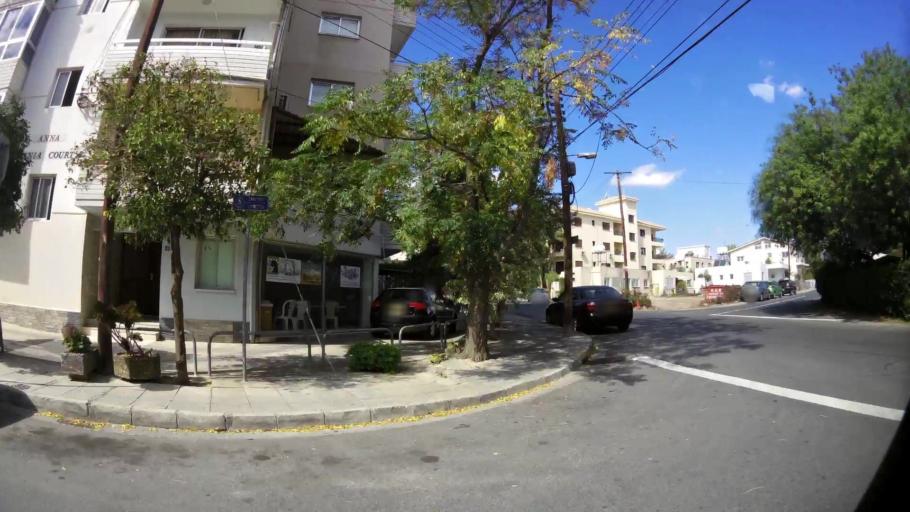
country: CY
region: Lefkosia
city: Nicosia
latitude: 35.1421
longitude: 33.3721
